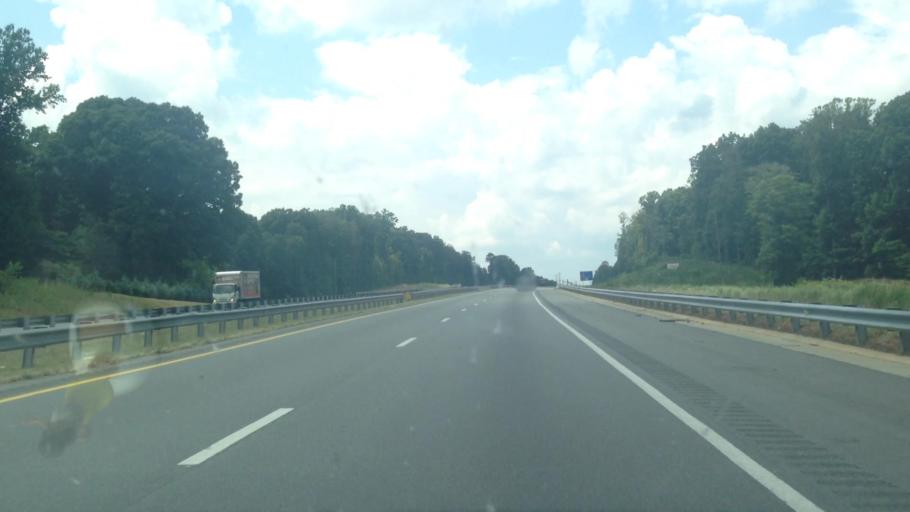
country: US
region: North Carolina
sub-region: Forsyth County
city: Tobaccoville
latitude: 36.2397
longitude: -80.3434
